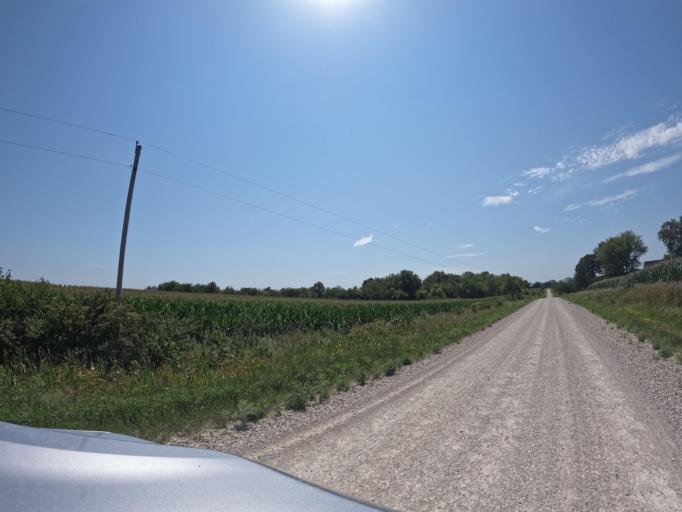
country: US
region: Iowa
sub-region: Henry County
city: Mount Pleasant
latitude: 40.8900
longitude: -91.6479
